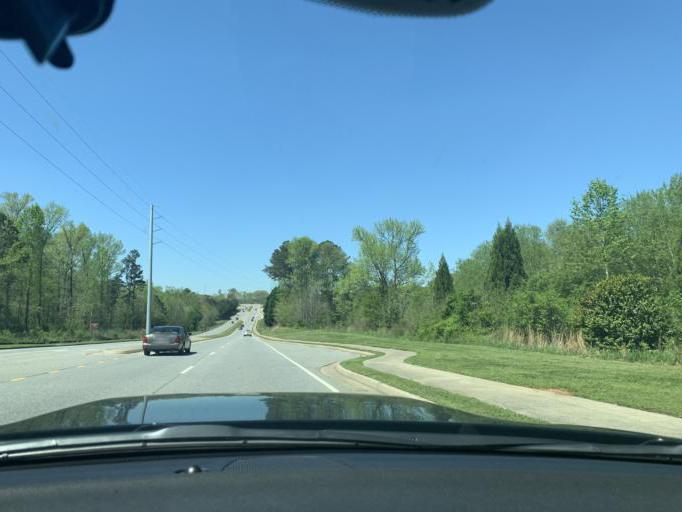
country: US
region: Georgia
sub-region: Forsyth County
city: Cumming
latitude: 34.1551
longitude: -84.1569
